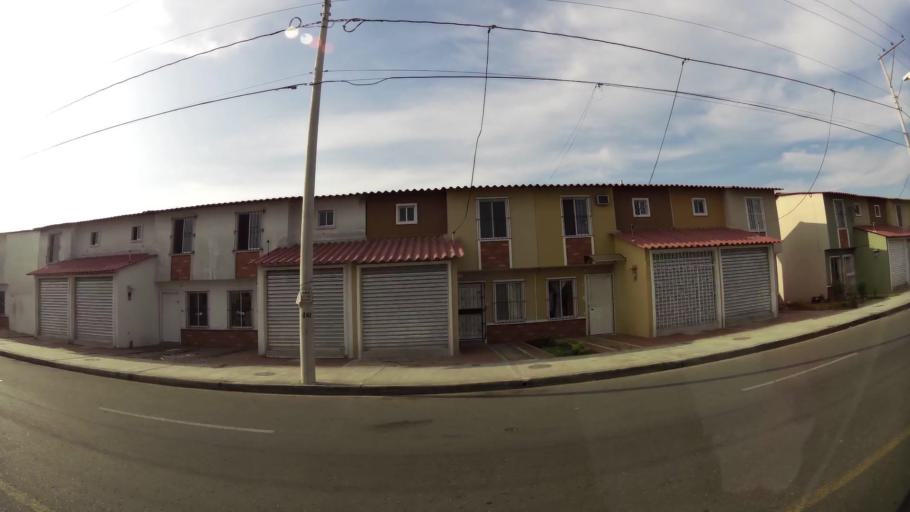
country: EC
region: Guayas
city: Eloy Alfaro
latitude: -2.0629
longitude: -79.8933
